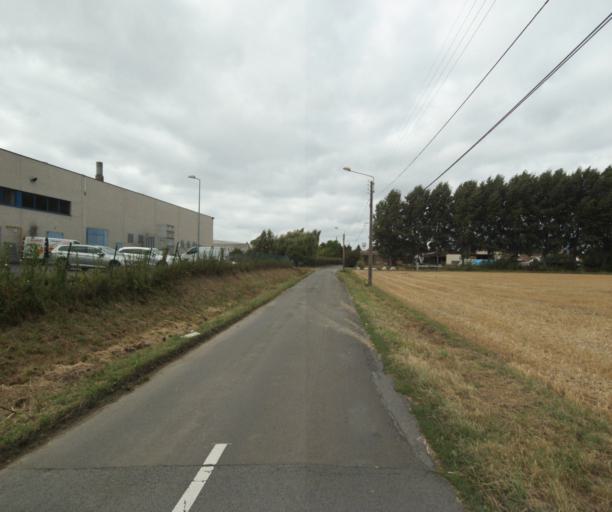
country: FR
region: Nord-Pas-de-Calais
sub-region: Departement du Nord
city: Leers
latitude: 50.6726
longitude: 3.2410
